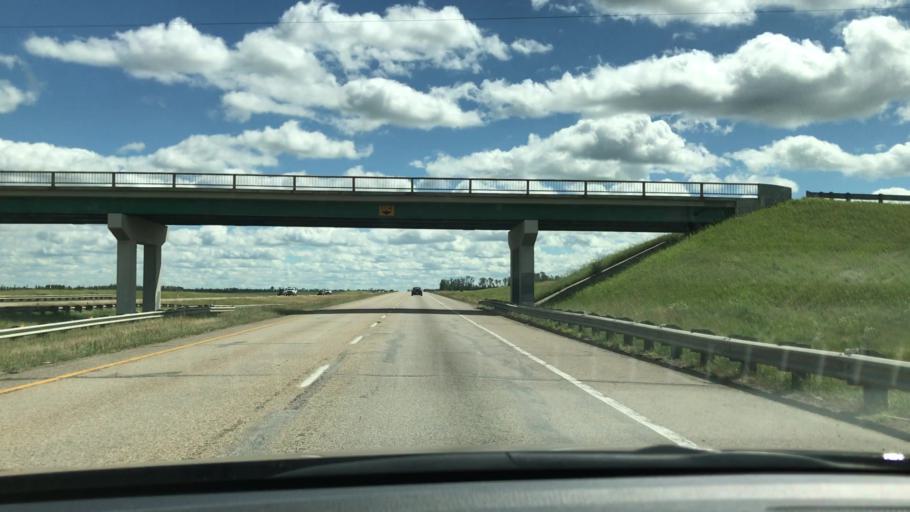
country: CA
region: Alberta
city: Millet
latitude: 53.1347
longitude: -113.5984
